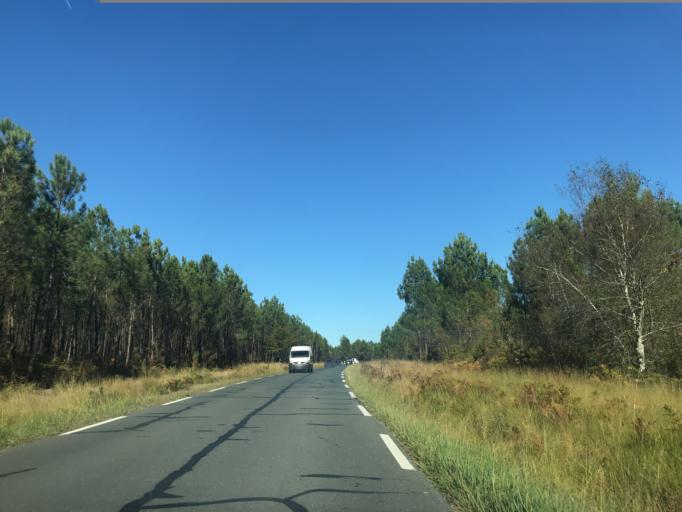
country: FR
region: Aquitaine
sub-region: Departement de la Gironde
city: Mios
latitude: 44.6383
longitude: -0.8868
